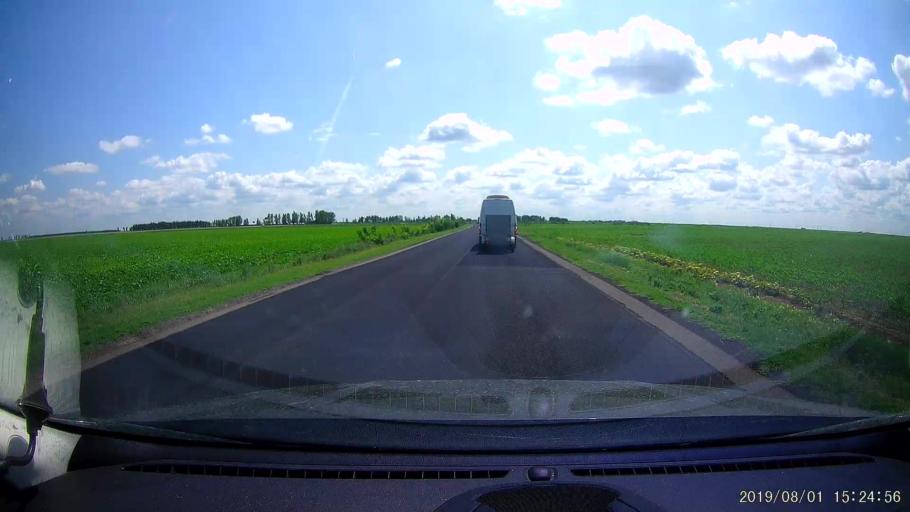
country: RO
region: Braila
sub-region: Comuna Viziru
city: Lanurile
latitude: 45.0281
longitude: 27.7428
